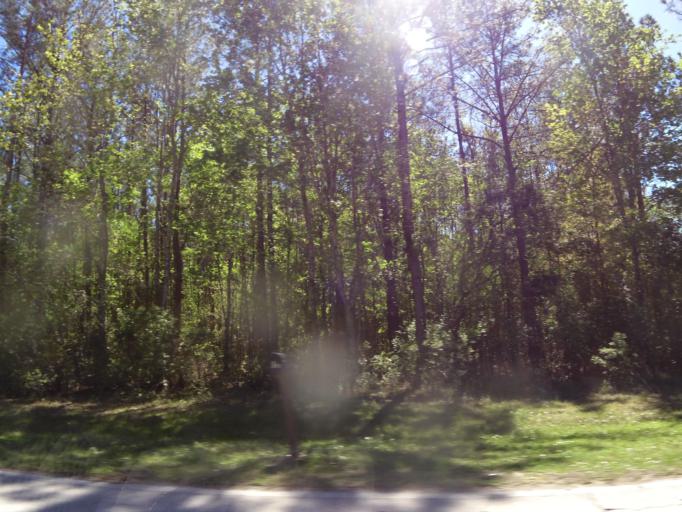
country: US
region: Florida
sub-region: Bradford County
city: Starke
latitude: 30.0559
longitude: -82.0636
